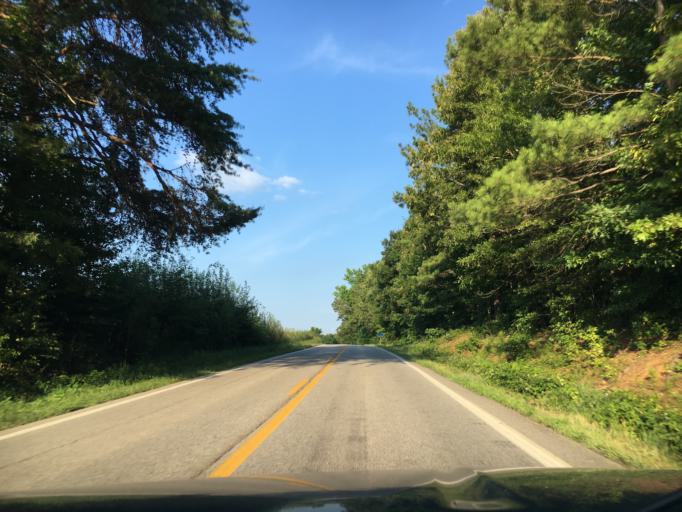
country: US
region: Virginia
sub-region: Pittsylvania County
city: Chatham
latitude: 36.8280
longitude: -79.2937
